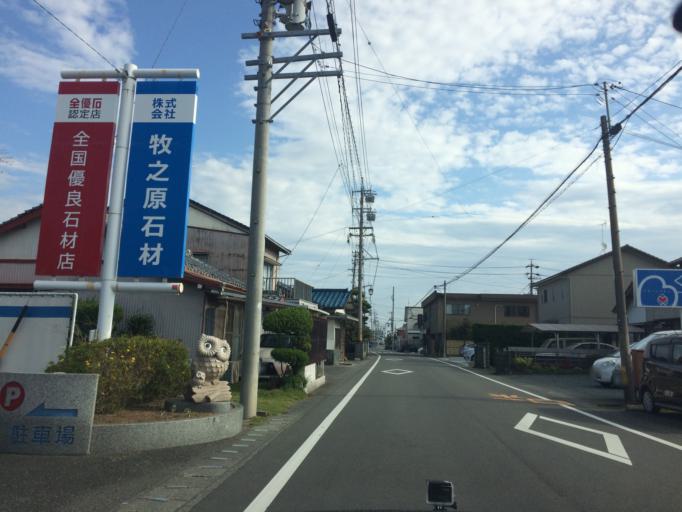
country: JP
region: Shizuoka
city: Sagara
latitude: 34.7498
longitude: 138.2333
